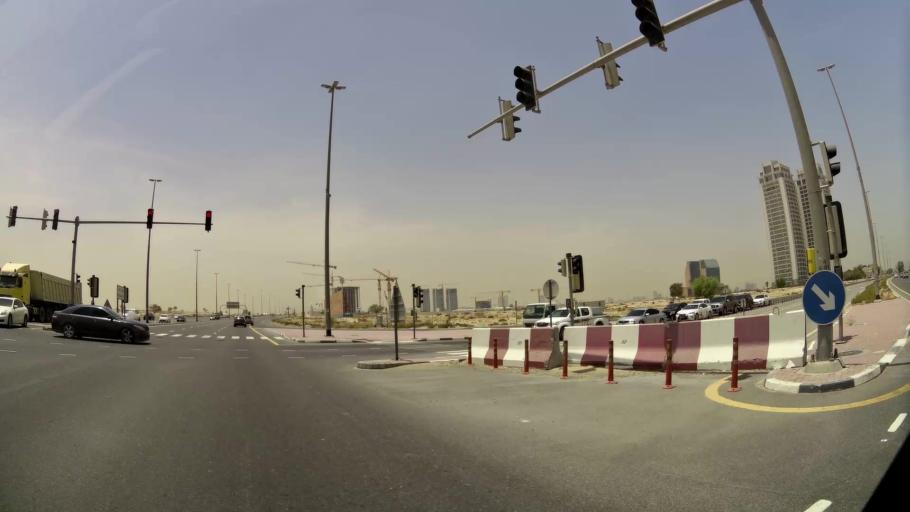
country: AE
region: Dubai
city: Dubai
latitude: 25.0814
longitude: 55.2498
